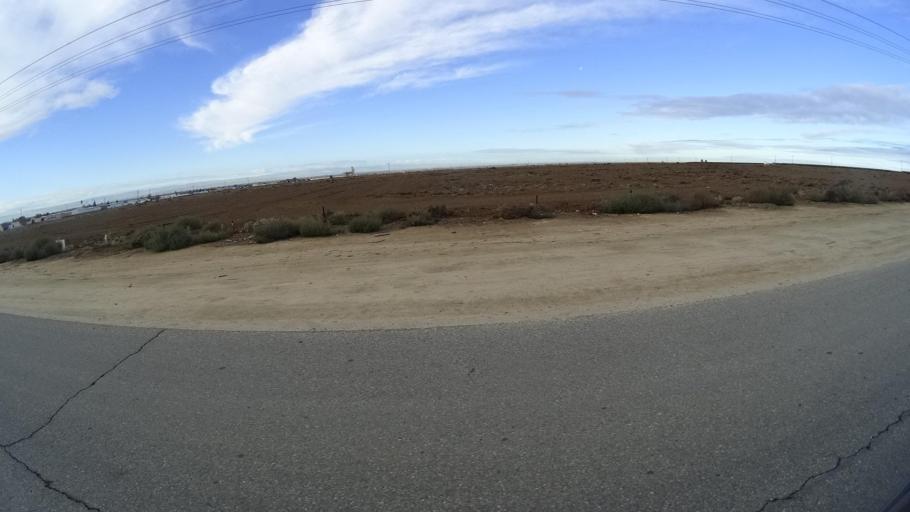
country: US
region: California
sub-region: Kern County
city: Oildale
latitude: 35.4528
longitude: -119.0822
